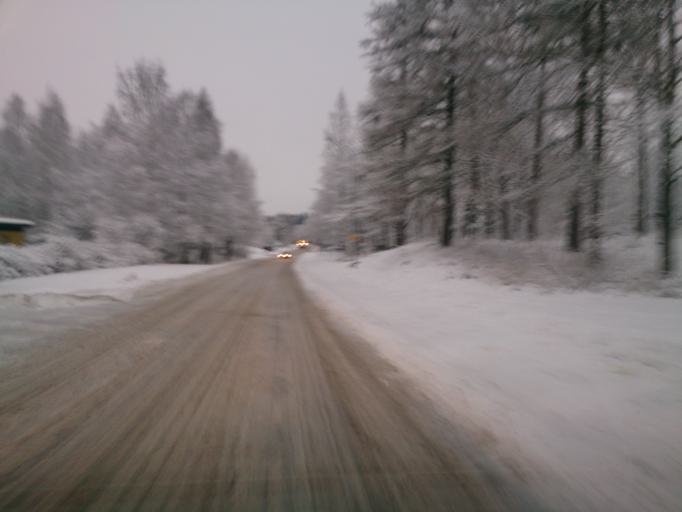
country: SE
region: OEstergoetland
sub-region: Atvidabergs Kommun
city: Atvidaberg
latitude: 58.1977
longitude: 15.9838
